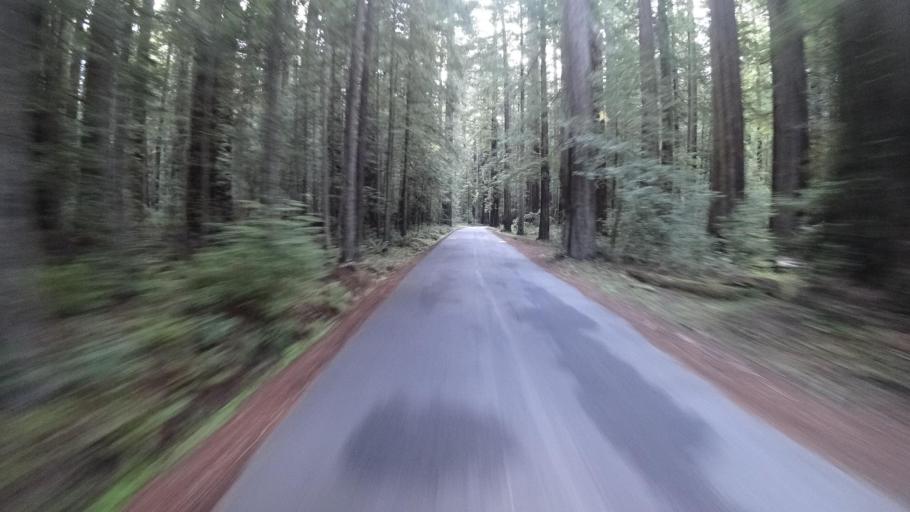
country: US
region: California
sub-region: Humboldt County
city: Rio Dell
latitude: 40.3514
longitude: -124.0043
